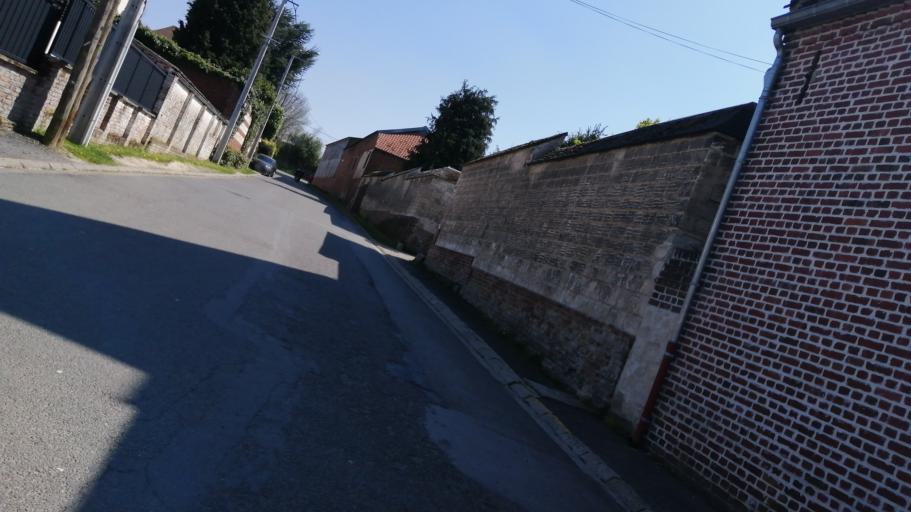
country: FR
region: Nord-Pas-de-Calais
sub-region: Departement du Pas-de-Calais
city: Duisans
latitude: 50.3073
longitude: 2.6569
